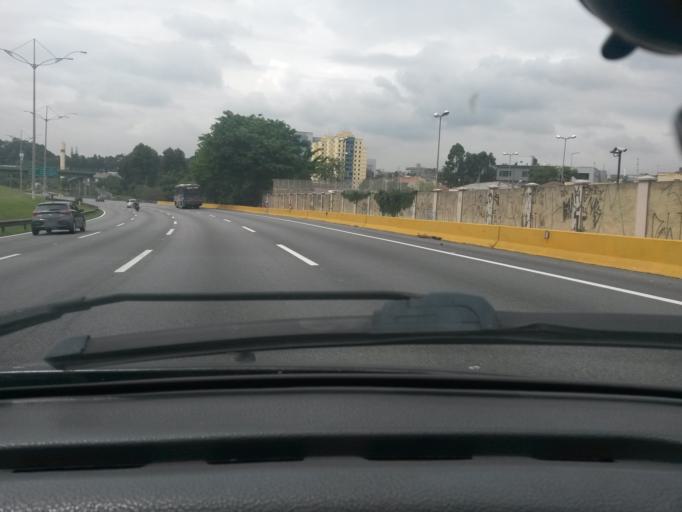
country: BR
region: Sao Paulo
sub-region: Sao Caetano Do Sul
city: Sao Caetano do Sul
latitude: -23.6360
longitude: -46.5954
